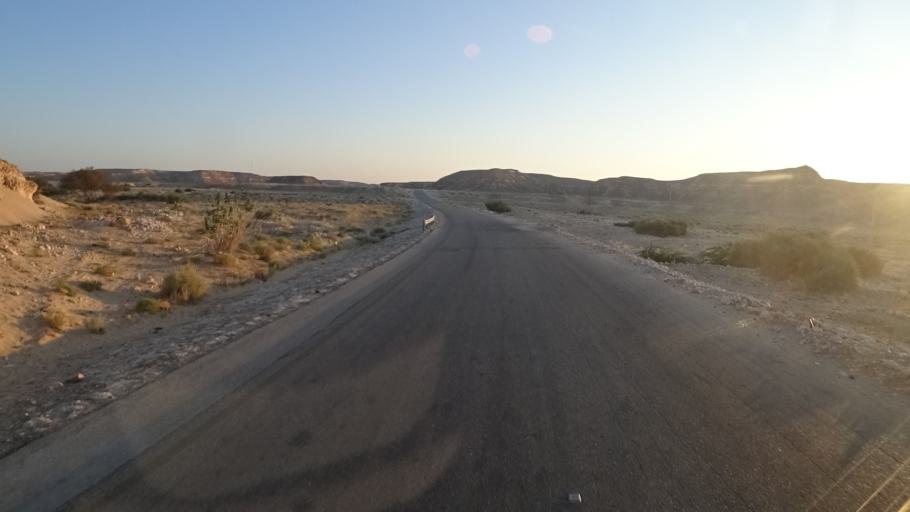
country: OM
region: Zufar
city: Salalah
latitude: 17.5059
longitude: 53.3639
